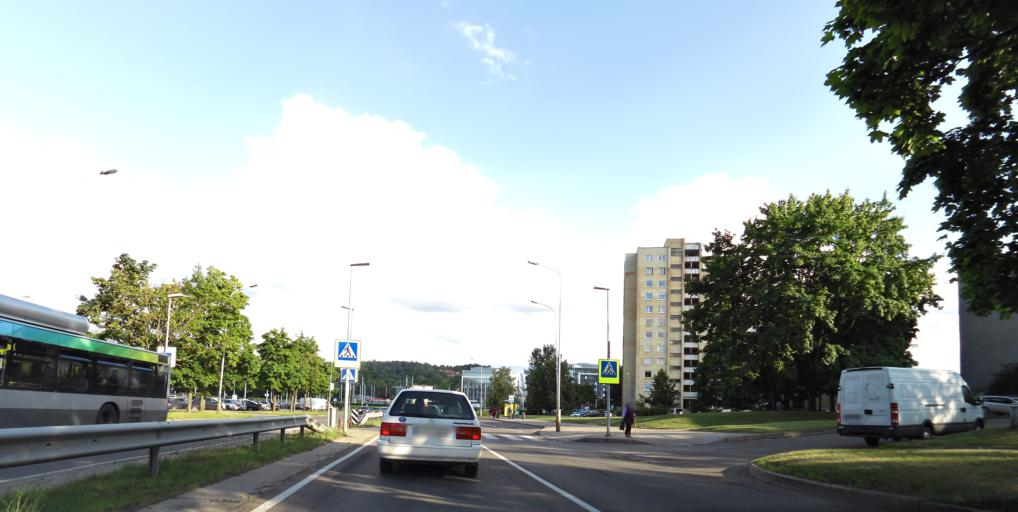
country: LT
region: Vilnius County
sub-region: Vilnius
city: Vilnius
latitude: 54.6975
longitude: 25.2966
